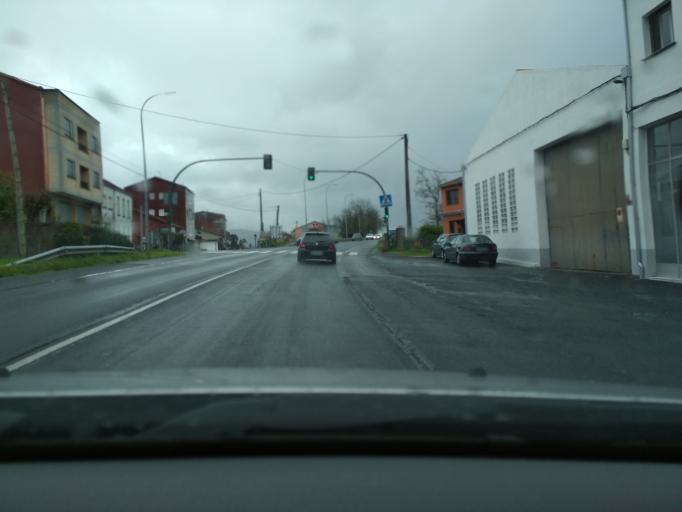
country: ES
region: Galicia
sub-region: Provincia da Coruna
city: Padron
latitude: 42.7521
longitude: -8.6534
